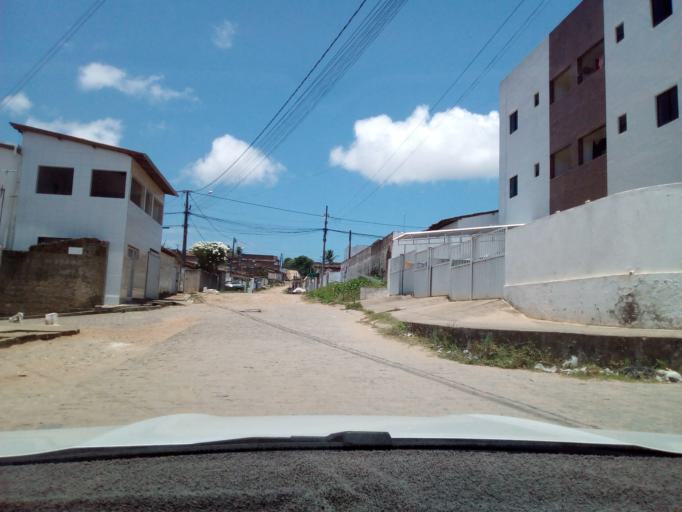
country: BR
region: Paraiba
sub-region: Joao Pessoa
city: Joao Pessoa
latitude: -7.1859
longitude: -34.8868
